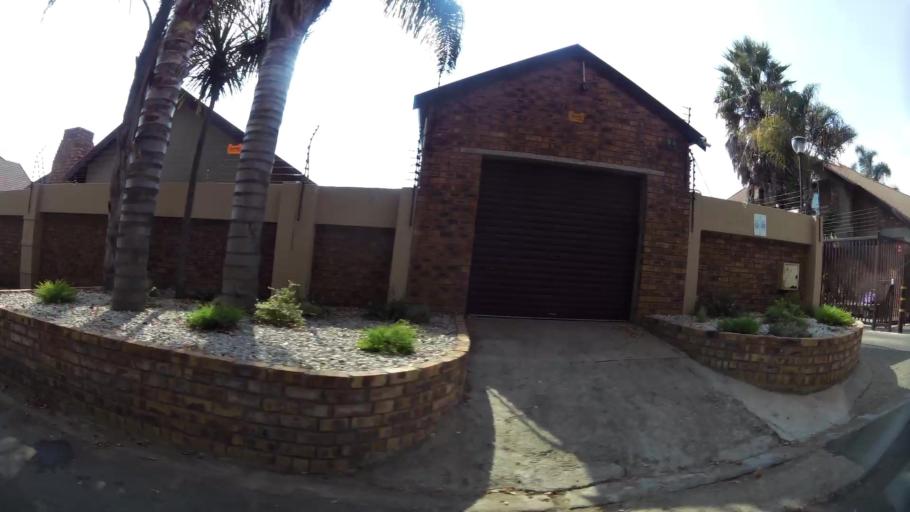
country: ZA
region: Gauteng
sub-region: City of Johannesburg Metropolitan Municipality
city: Modderfontein
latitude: -26.0877
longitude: 28.2307
